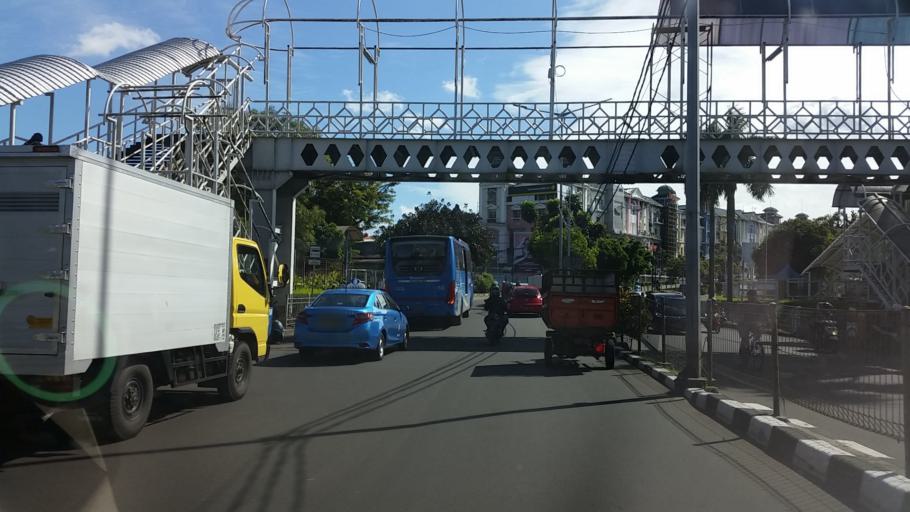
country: ID
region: Banten
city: South Tangerang
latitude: -6.2632
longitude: 106.7845
